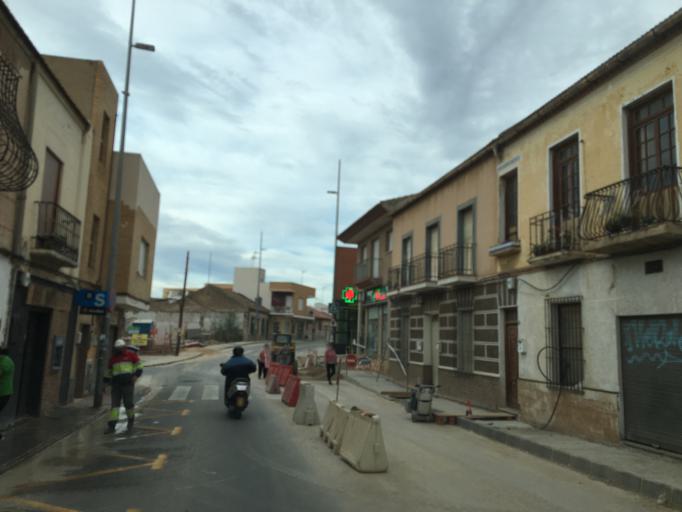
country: ES
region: Murcia
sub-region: Murcia
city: Cartagena
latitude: 37.6120
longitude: -1.0428
